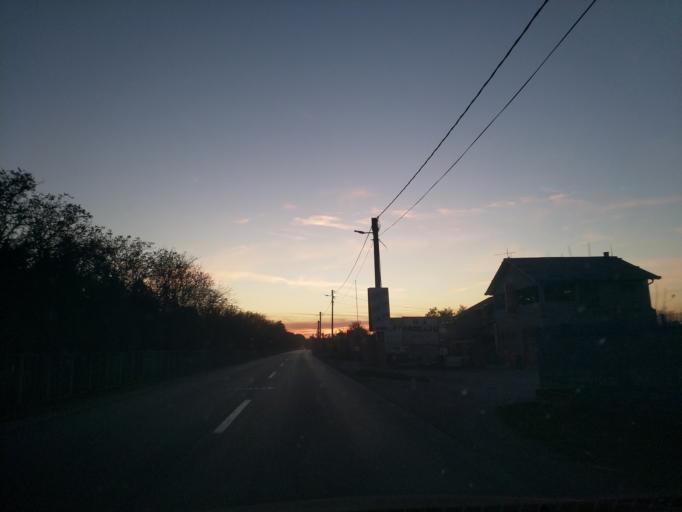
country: RS
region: Central Serbia
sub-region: Pomoravski Okrug
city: Svilajnac
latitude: 44.2271
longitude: 21.1665
